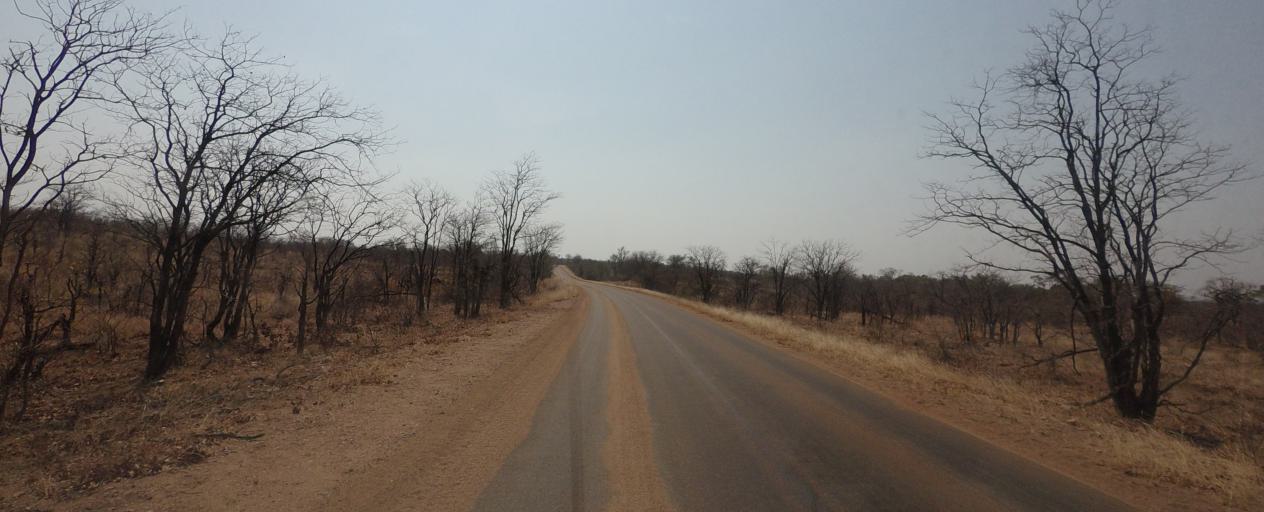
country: ZA
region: Limpopo
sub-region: Mopani District Municipality
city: Giyani
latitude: -23.2103
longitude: 31.3136
